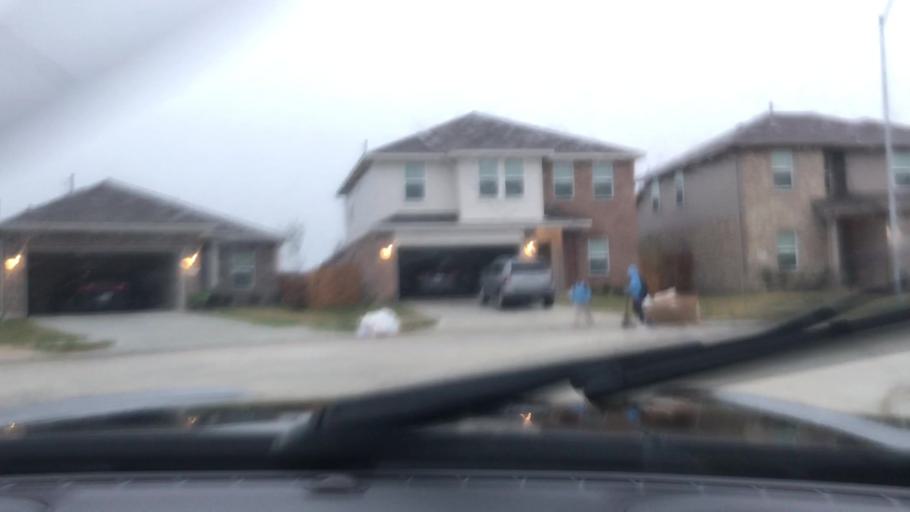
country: US
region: Texas
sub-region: Harris County
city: Humble
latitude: 30.0174
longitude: -95.3110
